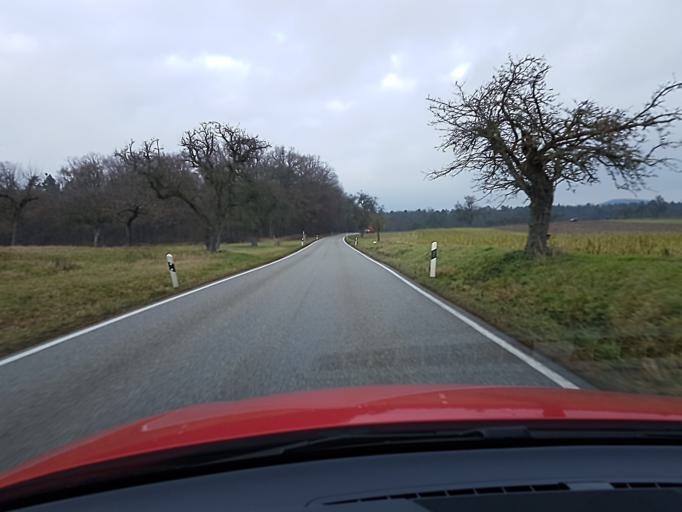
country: DE
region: Baden-Wuerttemberg
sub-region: Karlsruhe Region
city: Muhlacker
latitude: 48.9876
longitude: 8.8625
